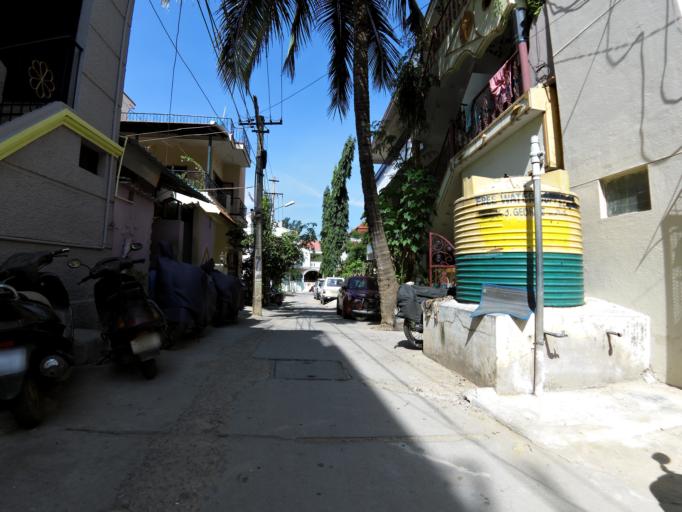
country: IN
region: Karnataka
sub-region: Bangalore Urban
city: Bangalore
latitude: 13.0028
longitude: 77.6280
